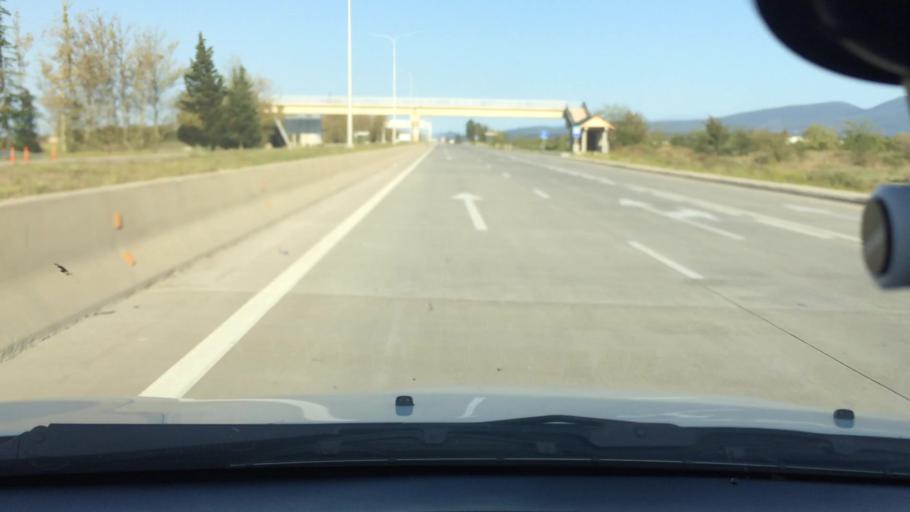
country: GE
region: Imereti
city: Zestap'oni
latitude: 42.1601
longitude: 42.9483
